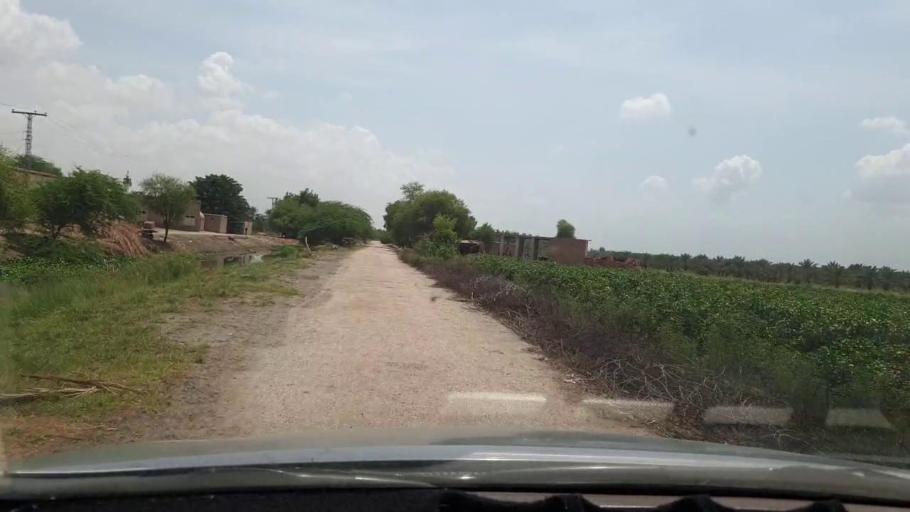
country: PK
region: Sindh
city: Khairpur
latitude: 27.4705
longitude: 68.7975
